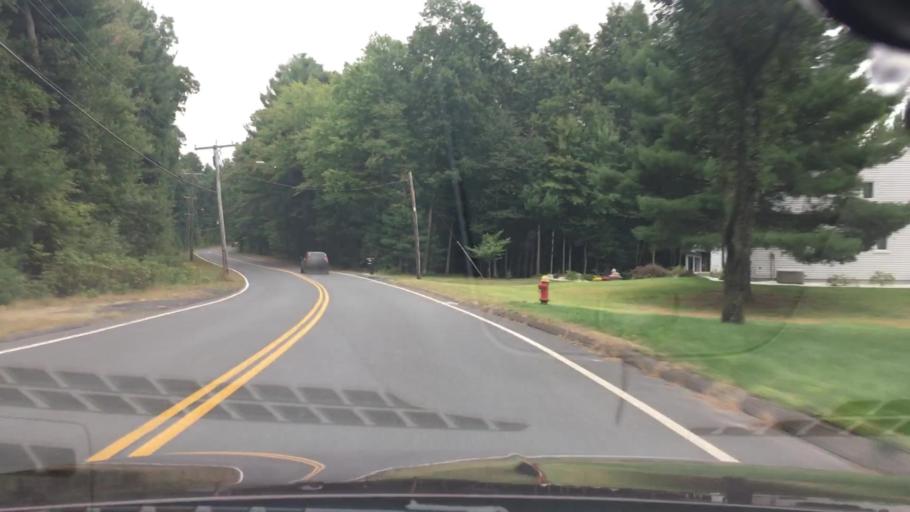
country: US
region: Connecticut
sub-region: Hartford County
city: Sherwood Manor
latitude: 42.0190
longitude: -72.5606
